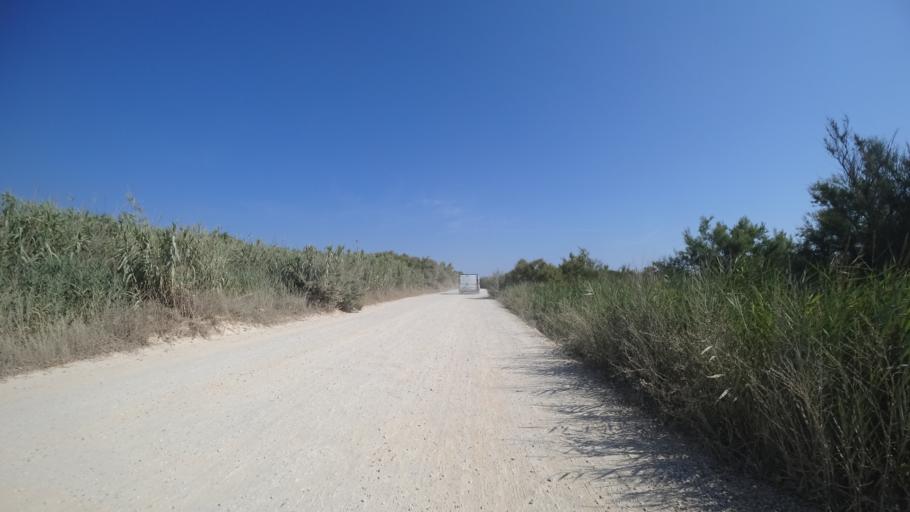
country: FR
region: Languedoc-Roussillon
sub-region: Departement des Pyrenees-Orientales
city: Le Barcares
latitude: 42.7703
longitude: 3.0355
